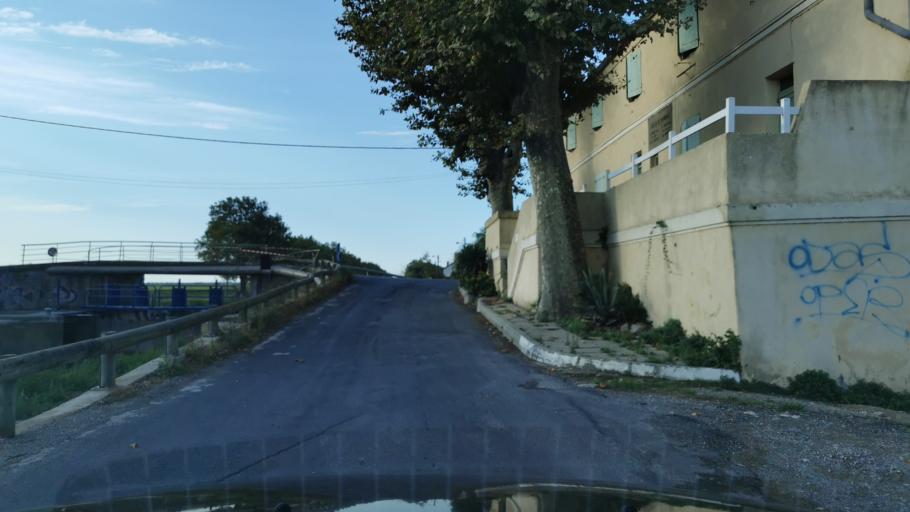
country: FR
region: Languedoc-Roussillon
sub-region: Departement de l'Aude
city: Gruissan
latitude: 43.1223
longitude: 3.0308
